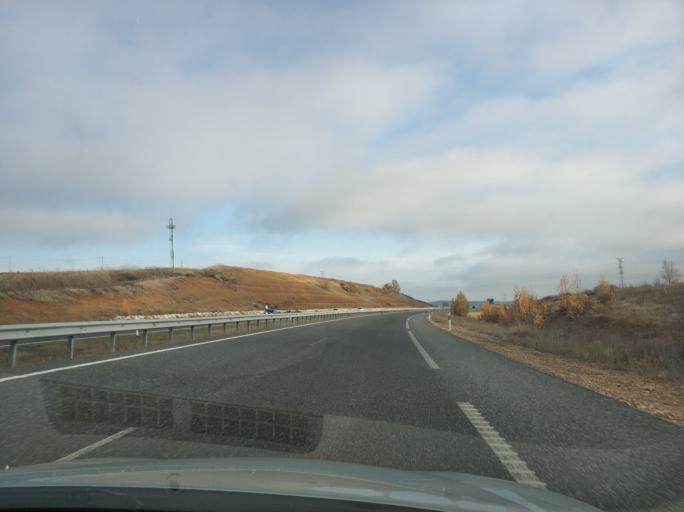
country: ES
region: Castille and Leon
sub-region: Provincia de Leon
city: Valdefresno
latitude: 42.5622
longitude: -5.4779
